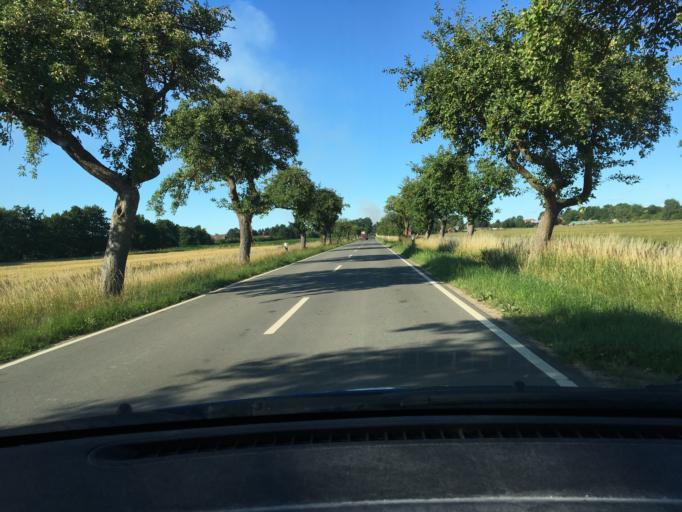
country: DE
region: Mecklenburg-Vorpommern
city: Boizenburg
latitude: 53.3492
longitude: 10.7009
